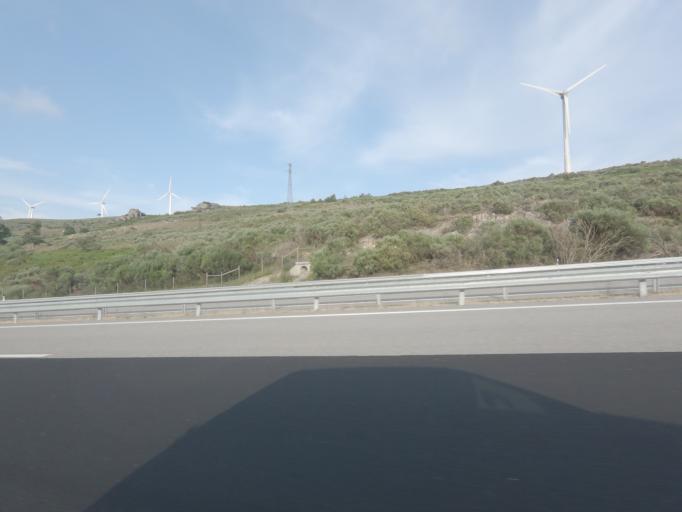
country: PT
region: Vila Real
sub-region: Vila Pouca de Aguiar
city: Vila Pouca de Aguiar
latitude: 41.4531
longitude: -7.6456
